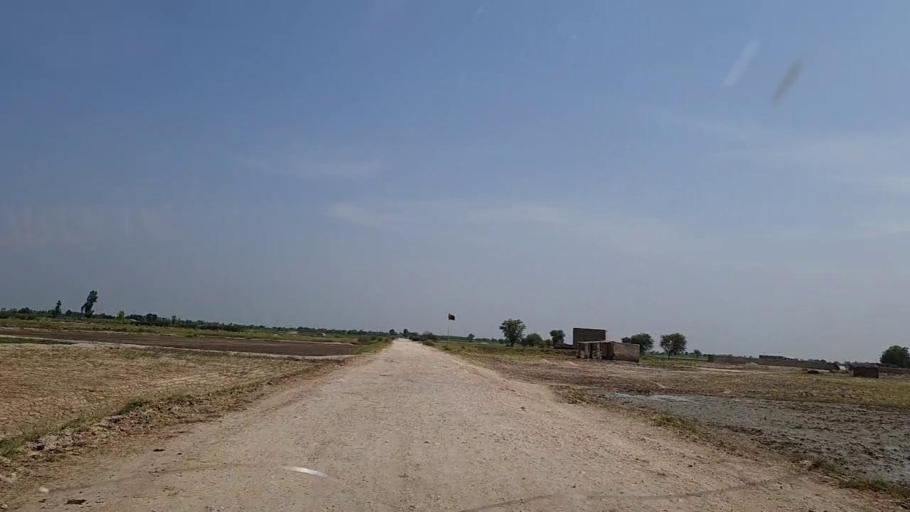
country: PK
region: Sindh
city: Khanpur
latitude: 27.7992
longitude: 69.3136
